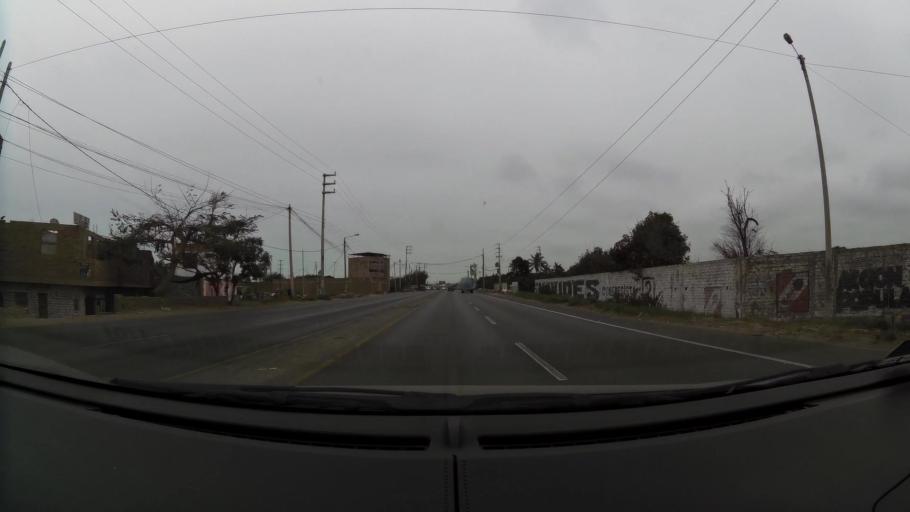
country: PE
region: La Libertad
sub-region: Provincia de Trujillo
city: Moche
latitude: -8.1708
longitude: -79.0025
